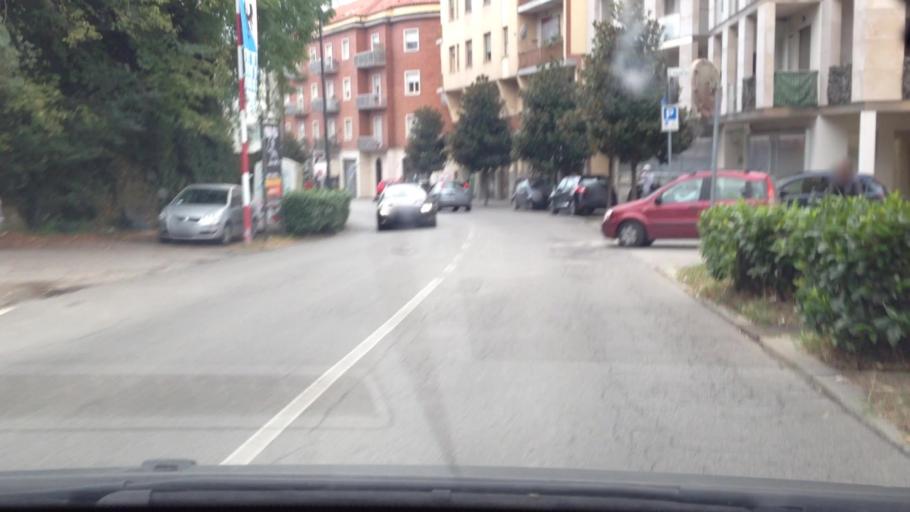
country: IT
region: Piedmont
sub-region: Provincia di Asti
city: Asti
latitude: 44.9028
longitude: 8.1967
